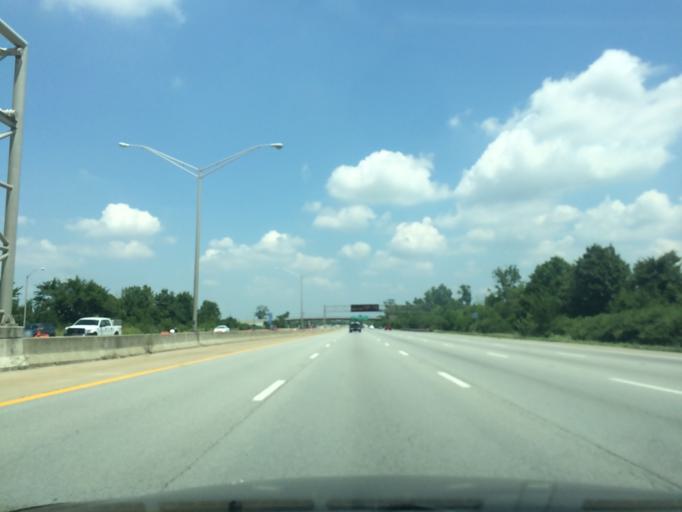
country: US
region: Kentucky
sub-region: Jefferson County
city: Okolona
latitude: 38.1638
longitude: -85.7207
